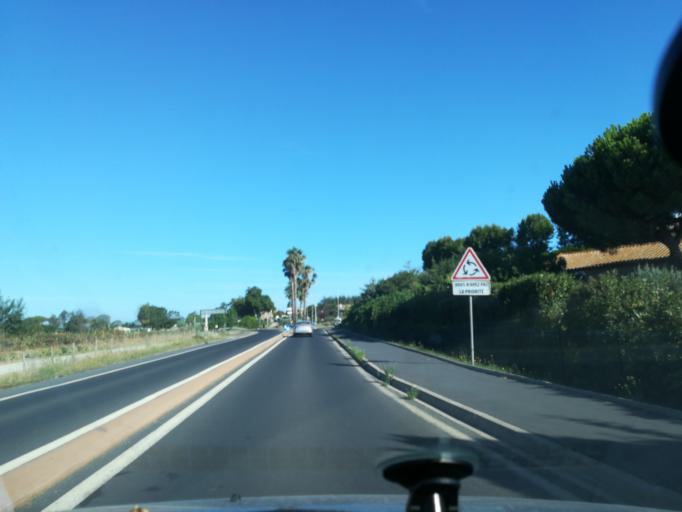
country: FR
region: Languedoc-Roussillon
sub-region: Departement de l'Herault
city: Portiragnes
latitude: 43.3029
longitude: 3.3321
